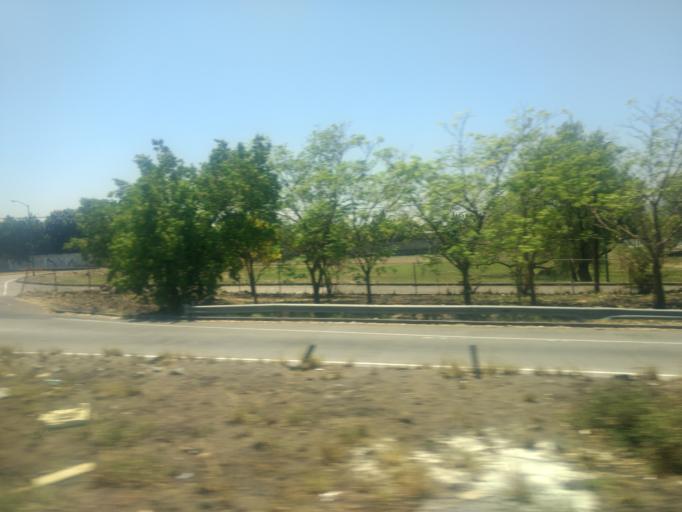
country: MX
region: Colima
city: Colima
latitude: 19.2346
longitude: -103.7040
